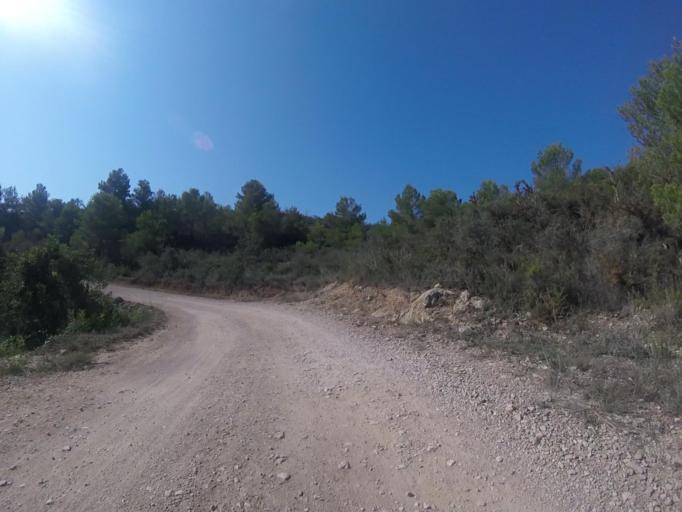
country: ES
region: Valencia
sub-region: Provincia de Castello
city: Santa Magdalena de Pulpis
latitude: 40.3278
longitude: 0.3534
